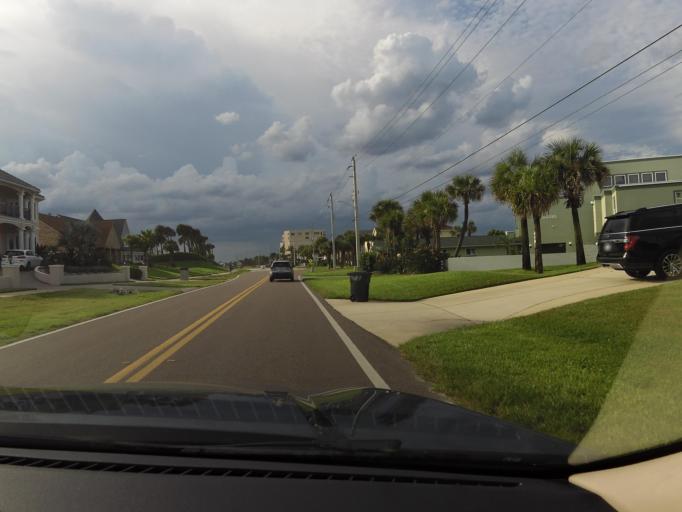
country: US
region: Florida
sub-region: Volusia County
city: Ponce Inlet
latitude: 29.0981
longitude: -80.9364
